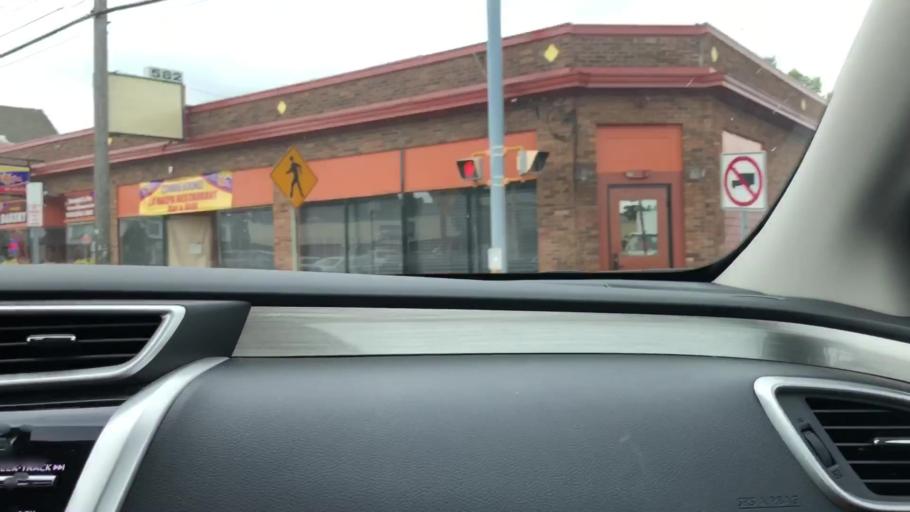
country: US
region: Rhode Island
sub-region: Providence County
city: Central Falls
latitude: 41.8786
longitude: -71.4153
